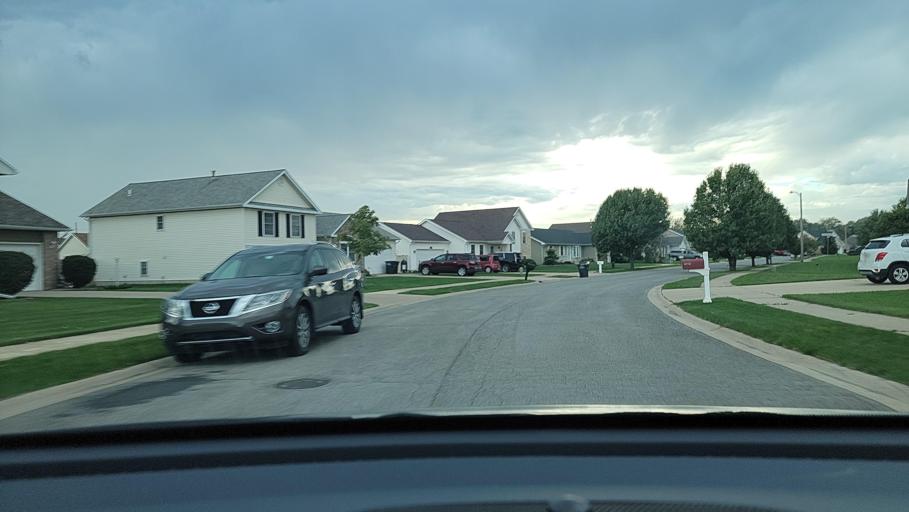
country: US
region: Indiana
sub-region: Porter County
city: Portage
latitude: 41.5624
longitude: -87.1607
